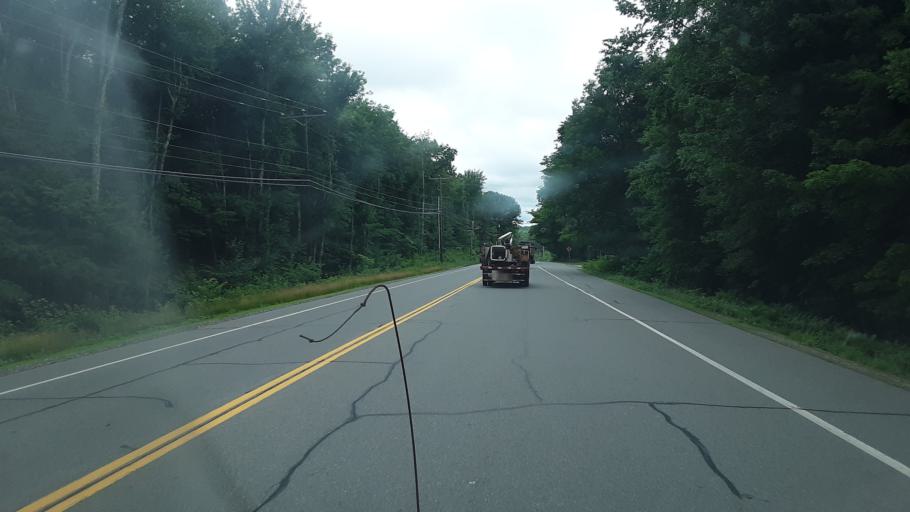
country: US
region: New Hampshire
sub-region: Rockingham County
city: Nottingham
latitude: 43.1693
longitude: -71.0879
